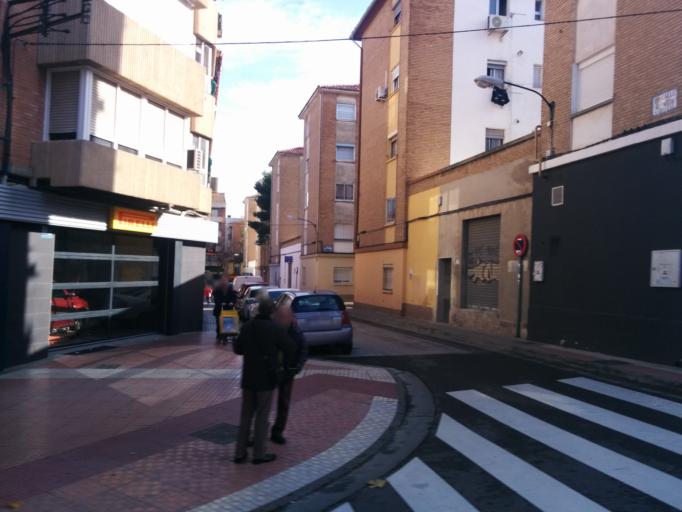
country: ES
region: Aragon
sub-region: Provincia de Zaragoza
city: Zaragoza
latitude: 41.6301
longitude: -0.8873
